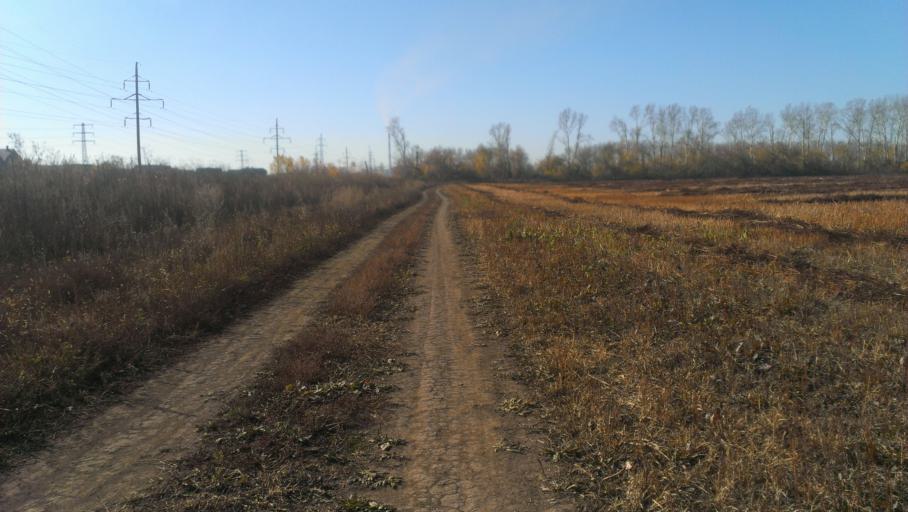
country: RU
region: Altai Krai
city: Novosilikatnyy
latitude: 53.3642
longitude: 83.6393
